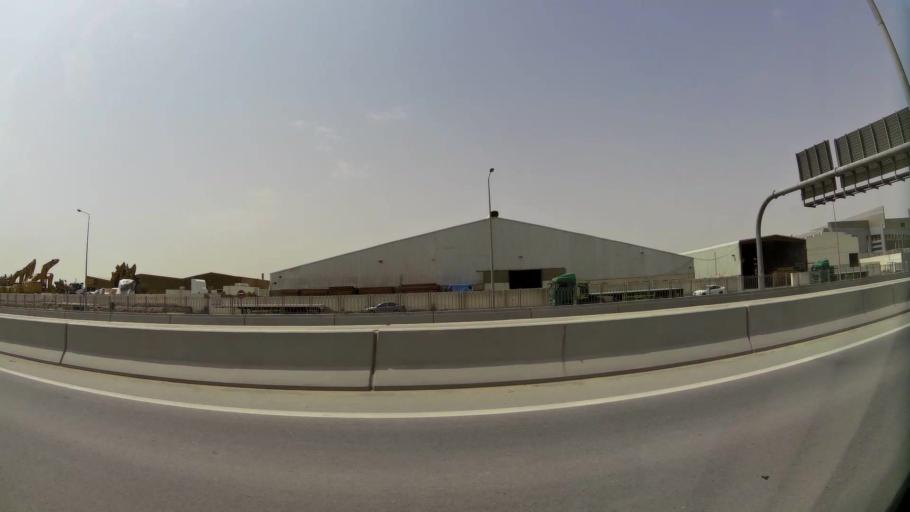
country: QA
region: Baladiyat ar Rayyan
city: Ar Rayyan
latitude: 25.2106
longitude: 51.4425
